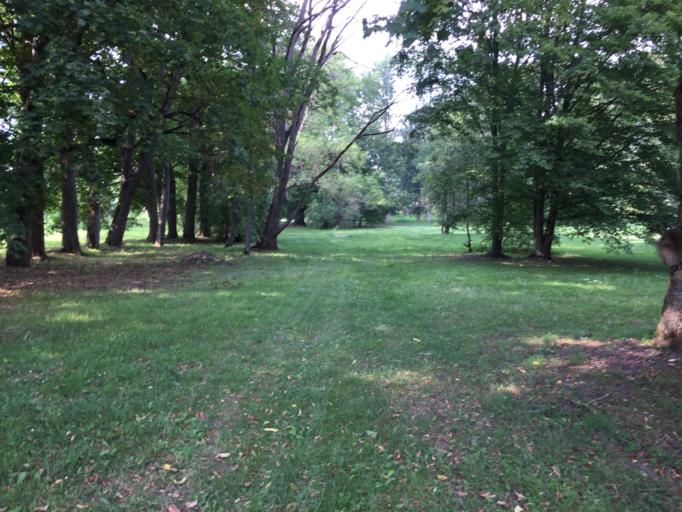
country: LV
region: Auces Novads
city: Auce
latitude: 56.4689
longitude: 22.8871
